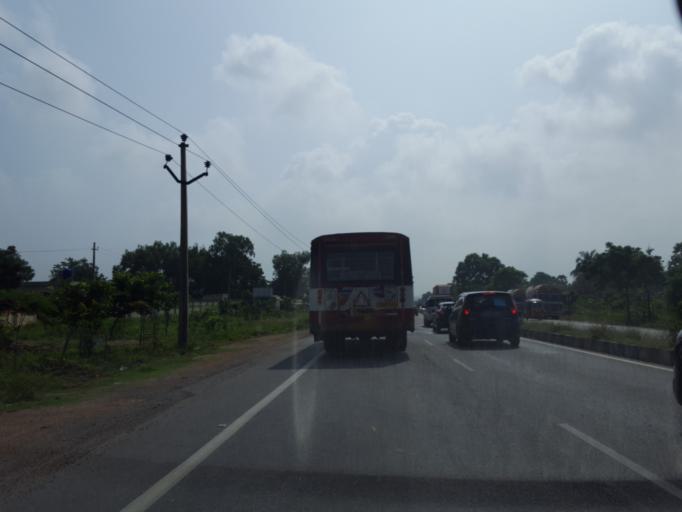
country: IN
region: Telangana
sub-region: Rangareddi
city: Ghatkesar
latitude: 17.3063
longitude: 78.7267
